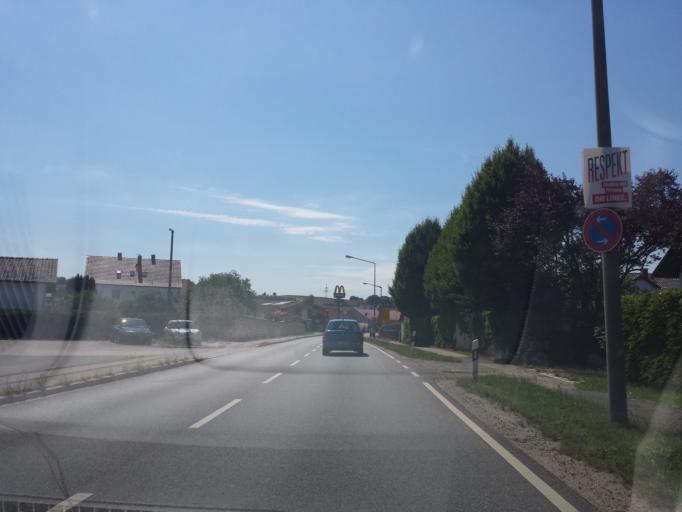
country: DE
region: Bavaria
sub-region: Upper Palatinate
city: Cham
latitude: 49.2041
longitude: 12.6649
